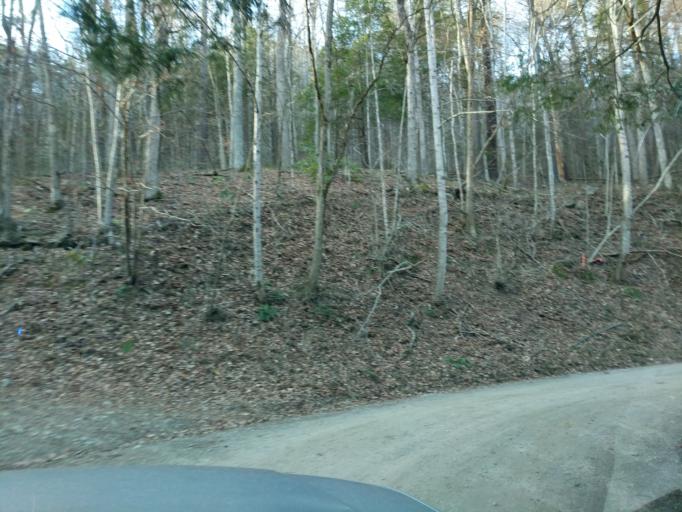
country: US
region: North Carolina
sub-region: Haywood County
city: Cove Creek
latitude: 35.7260
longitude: -83.0264
